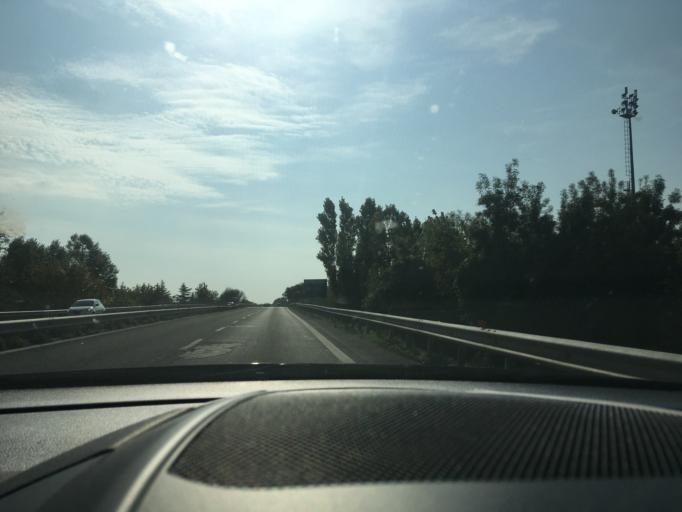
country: IT
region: Emilia-Romagna
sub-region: Forli-Cesena
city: San Mauro a Mare
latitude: 44.1464
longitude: 12.4505
